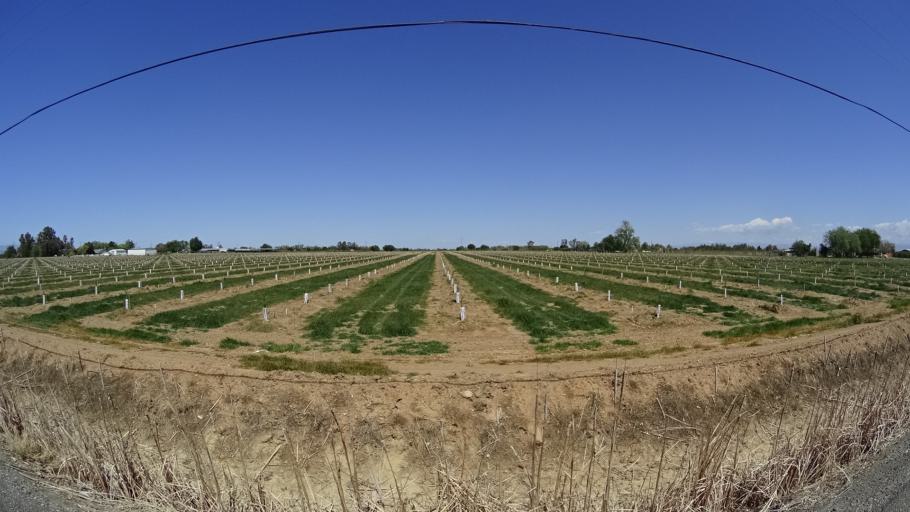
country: US
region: California
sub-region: Glenn County
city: Orland
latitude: 39.7868
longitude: -122.1937
